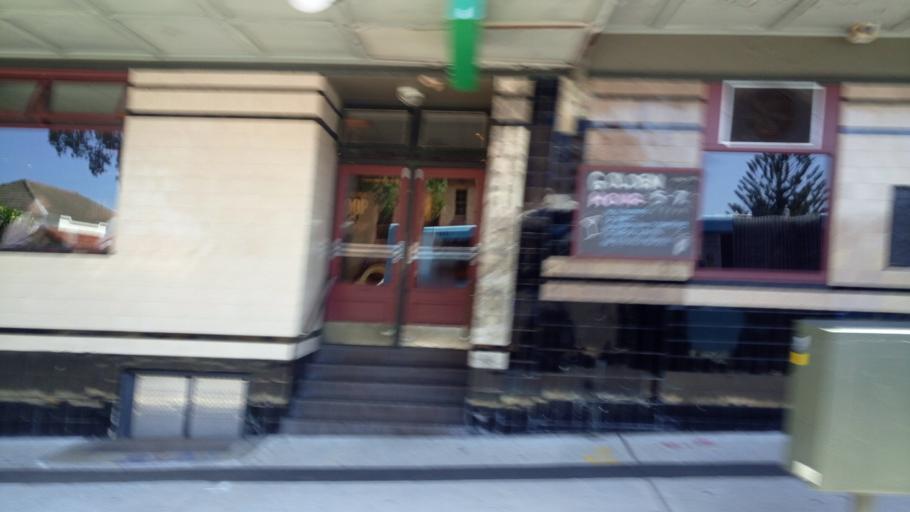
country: AU
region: New South Wales
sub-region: Waverley
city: Bondi
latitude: -33.8947
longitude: 151.2687
